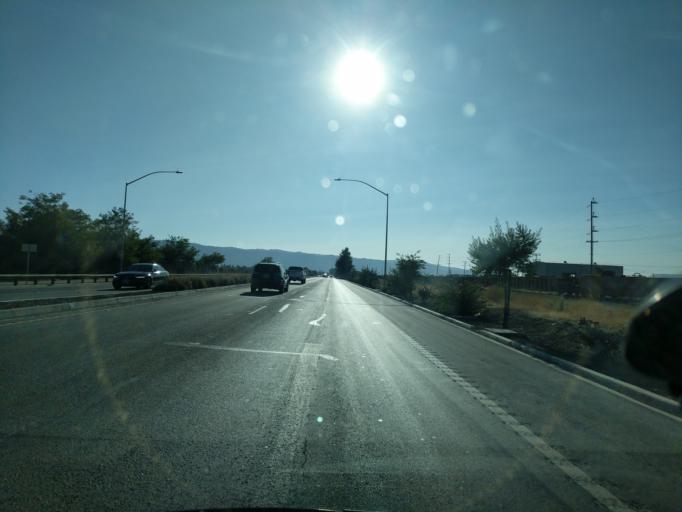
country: US
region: California
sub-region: Alameda County
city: Pleasanton
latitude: 37.6731
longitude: -121.8339
